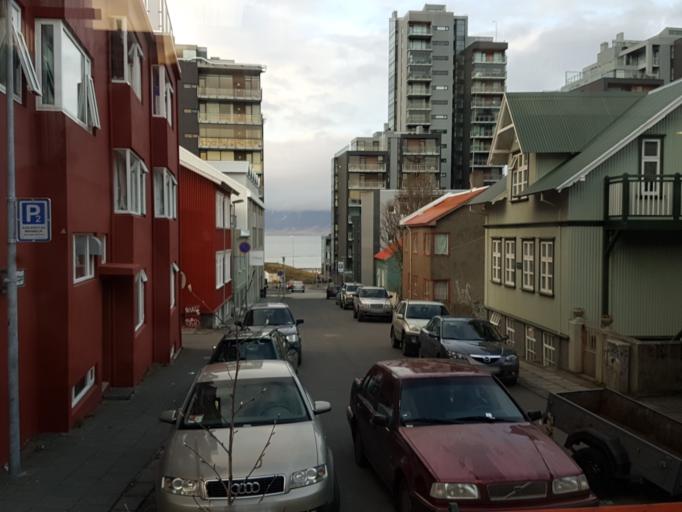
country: IS
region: Capital Region
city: Reykjavik
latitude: 64.1459
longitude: -21.9265
